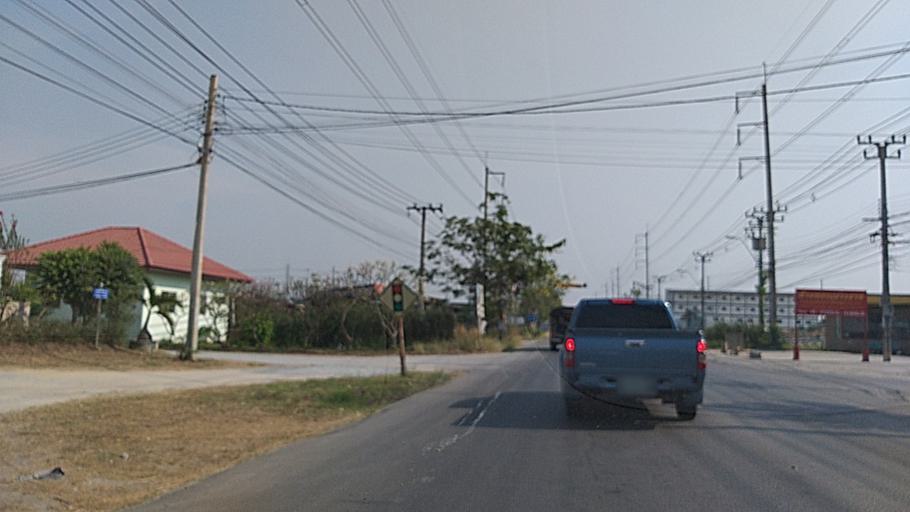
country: TH
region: Nonthaburi
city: Sai Noi
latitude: 14.0284
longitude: 100.3123
